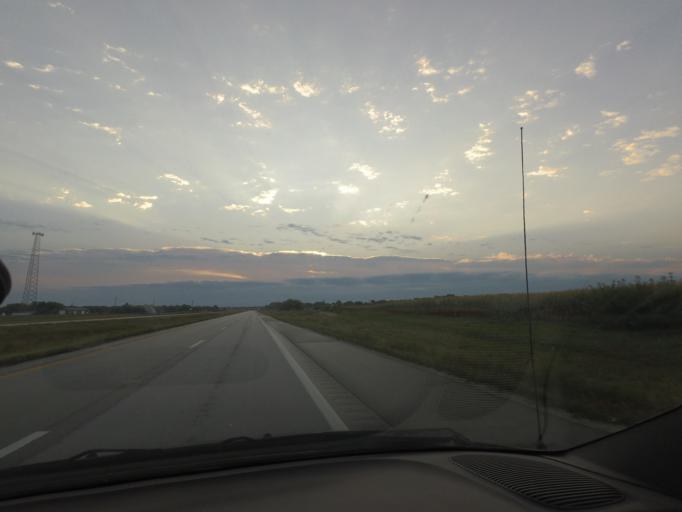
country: US
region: Missouri
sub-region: Macon County
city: Macon
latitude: 39.7503
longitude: -92.2720
